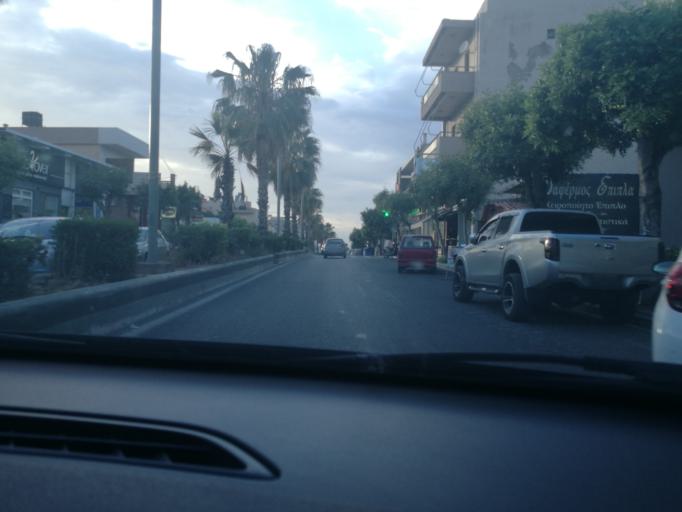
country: GR
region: Crete
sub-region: Nomos Irakleiou
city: Irakleion
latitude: 35.3160
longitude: 25.1468
